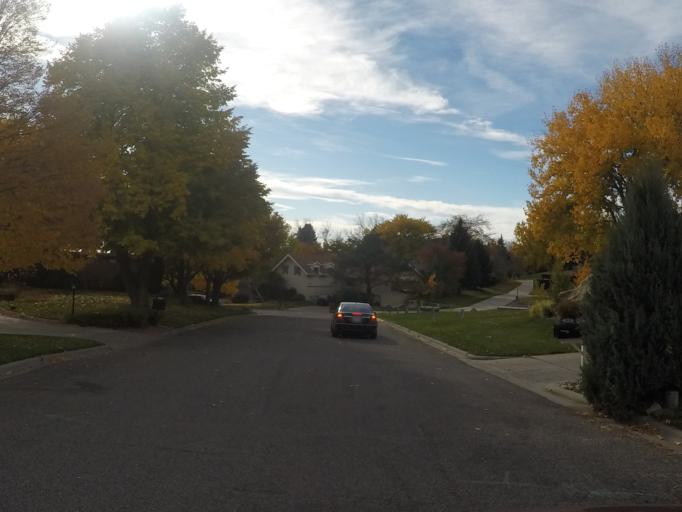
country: US
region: Montana
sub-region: Yellowstone County
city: Billings
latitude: 45.8010
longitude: -108.5584
